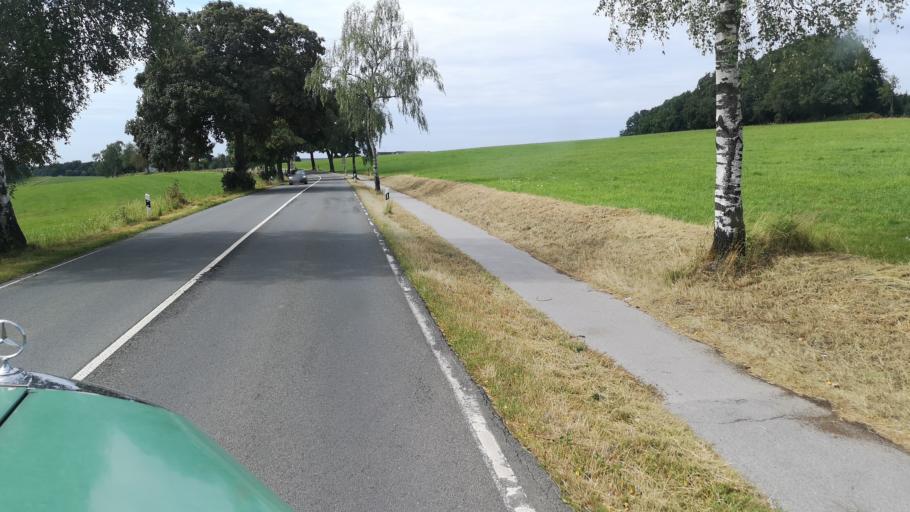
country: DE
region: North Rhine-Westphalia
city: Huckeswagen
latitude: 51.1713
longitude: 7.3615
